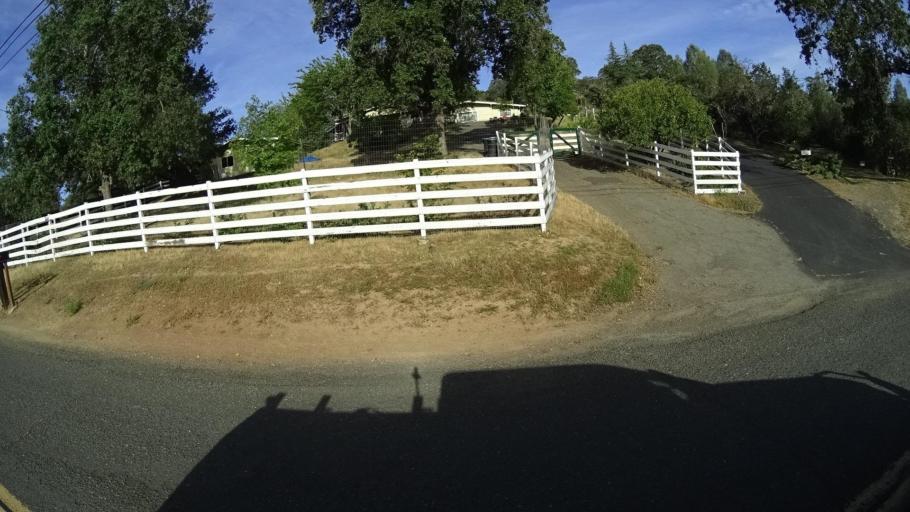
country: US
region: California
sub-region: Lake County
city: North Lakeport
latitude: 39.0728
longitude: -122.9199
